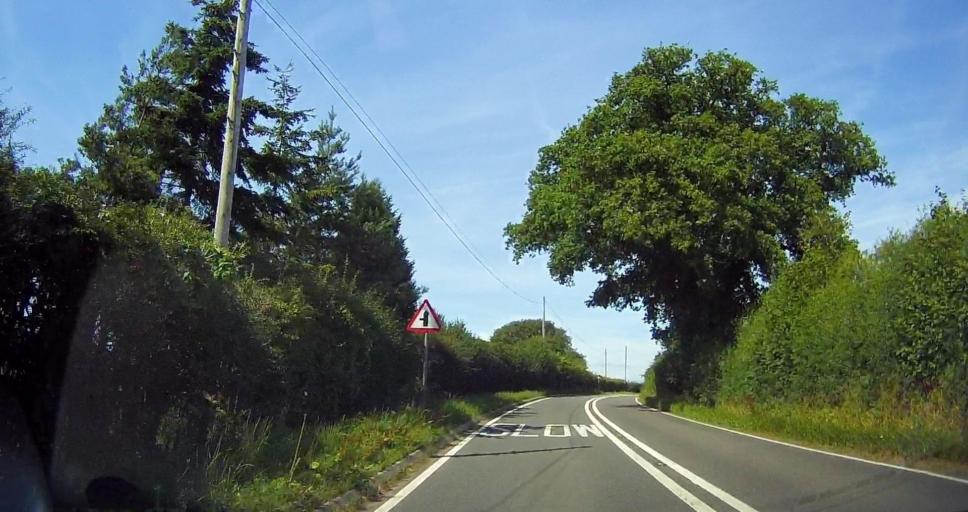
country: GB
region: England
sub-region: Shropshire
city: Market Drayton
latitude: 52.9179
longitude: -2.4968
